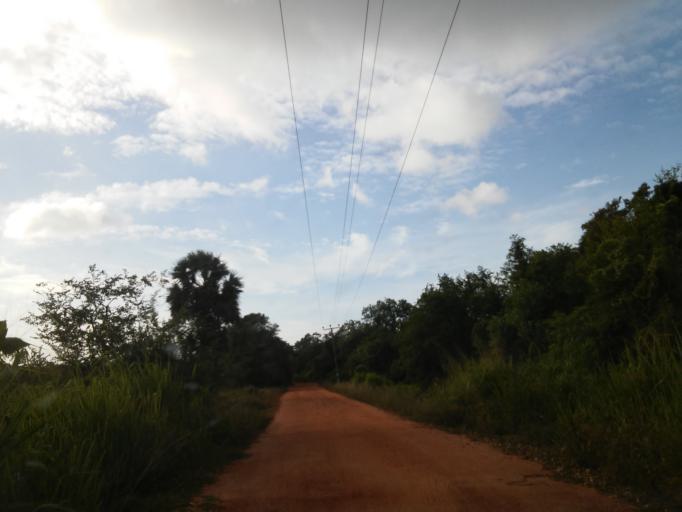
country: LK
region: Central
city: Sigiriya
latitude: 8.1708
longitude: 80.6820
